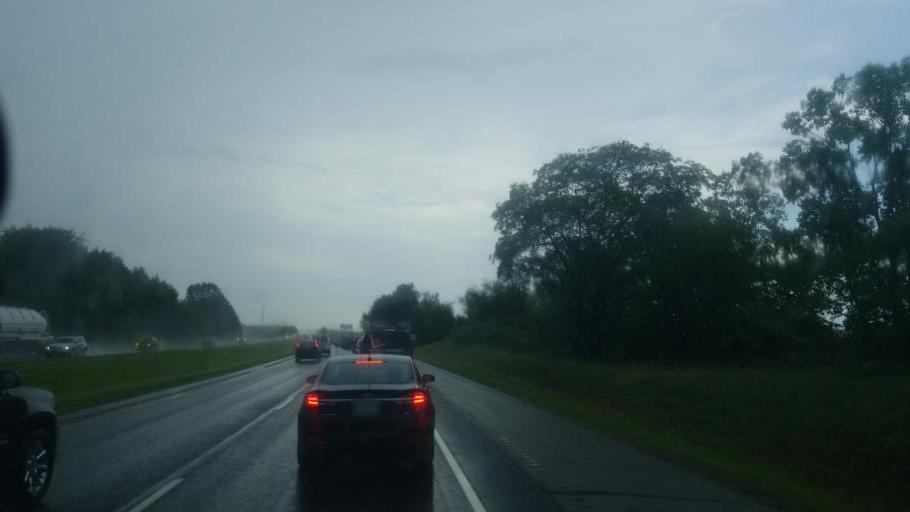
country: US
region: Indiana
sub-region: Whitley County
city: Columbia City
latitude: 41.1688
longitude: -85.4781
